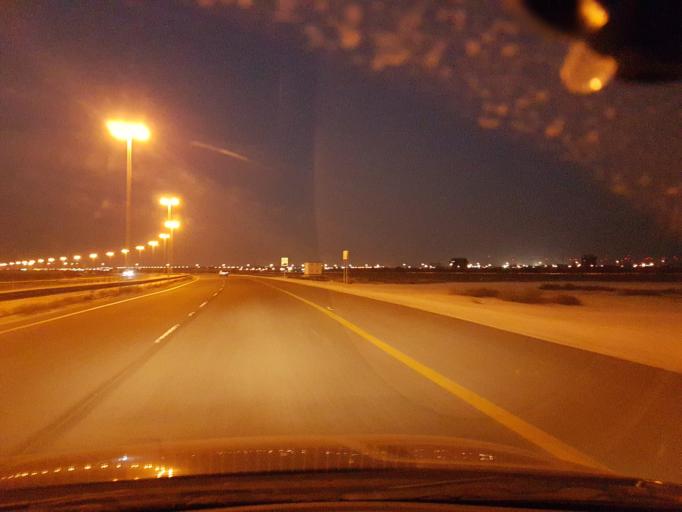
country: BH
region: Central Governorate
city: Dar Kulayb
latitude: 26.0296
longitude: 50.4985
